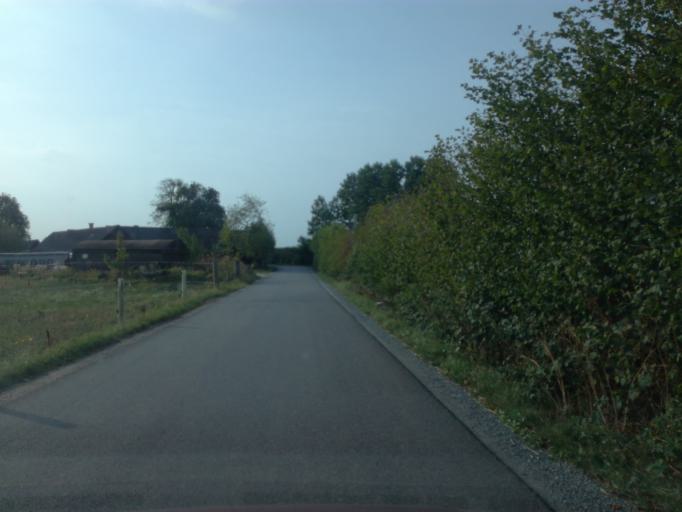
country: DK
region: South Denmark
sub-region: Vejle Kommune
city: Borkop
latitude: 55.6436
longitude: 9.5794
